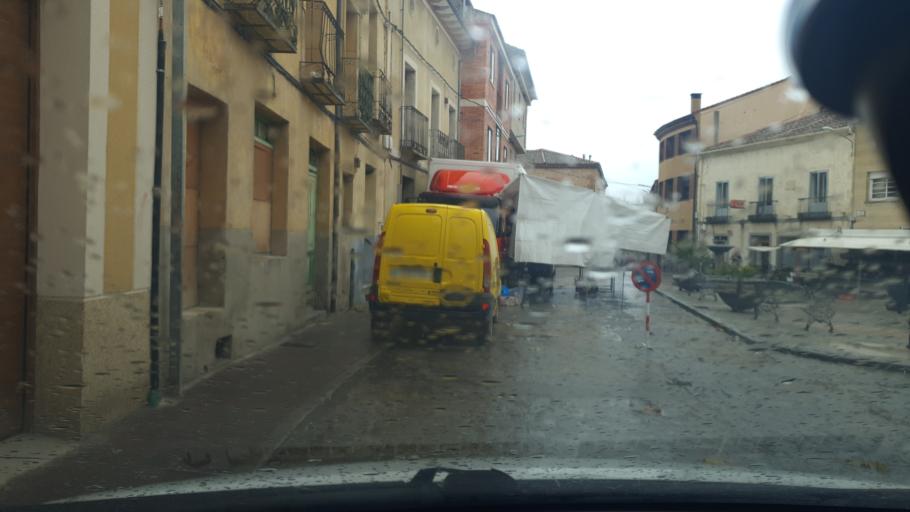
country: ES
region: Castille and Leon
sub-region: Provincia de Segovia
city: Carbonero el Mayor
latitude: 41.1220
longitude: -4.2654
